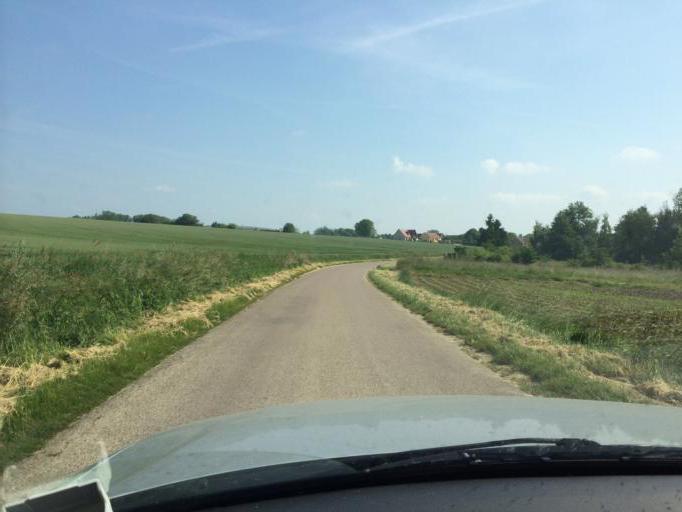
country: FR
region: Bourgogne
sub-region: Departement de l'Yonne
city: Fleury-la-Vallee
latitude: 47.8780
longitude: 3.4048
